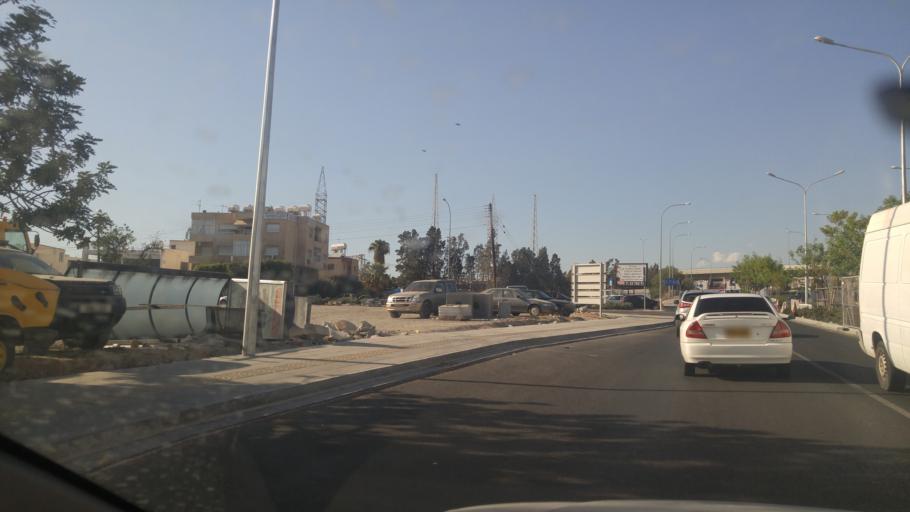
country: CY
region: Limassol
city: Limassol
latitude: 34.7027
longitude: 33.0279
